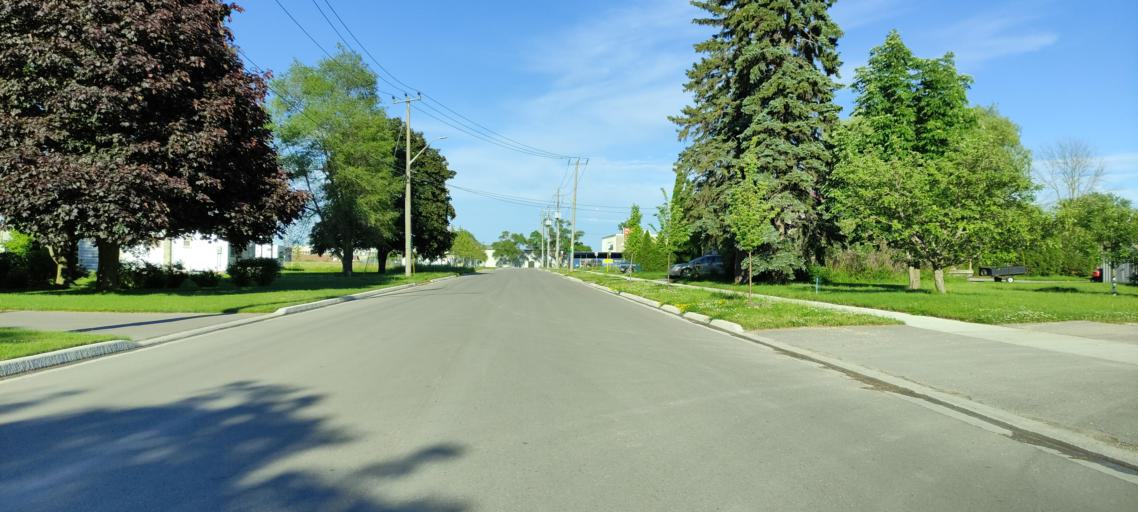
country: CA
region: Ontario
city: Stratford
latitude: 43.3653
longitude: -80.9604
